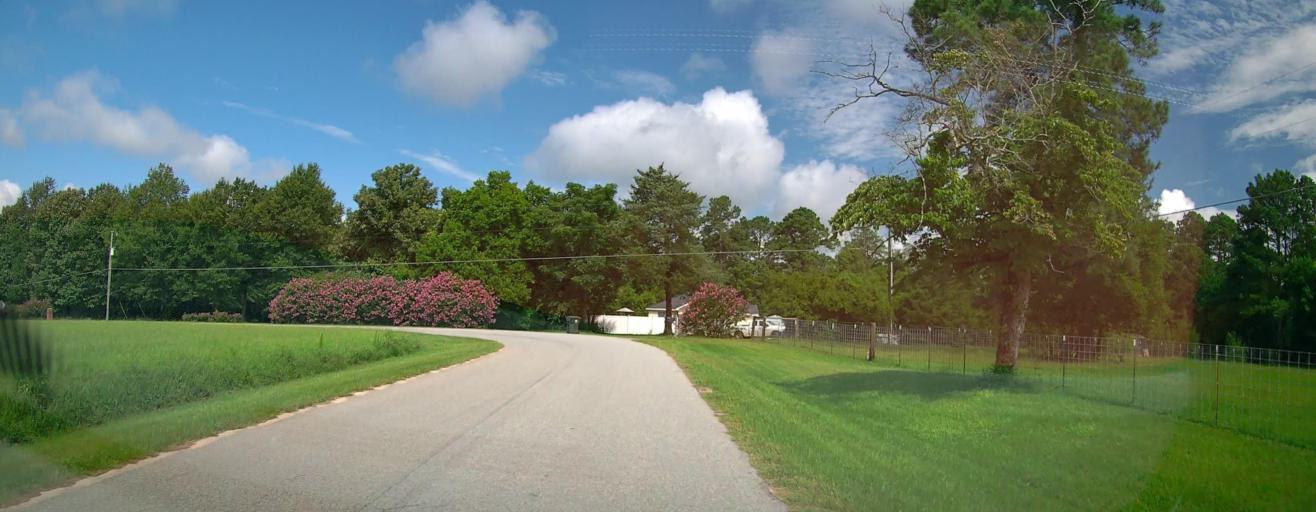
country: US
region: Georgia
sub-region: Peach County
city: Byron
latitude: 32.6625
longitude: -83.7777
